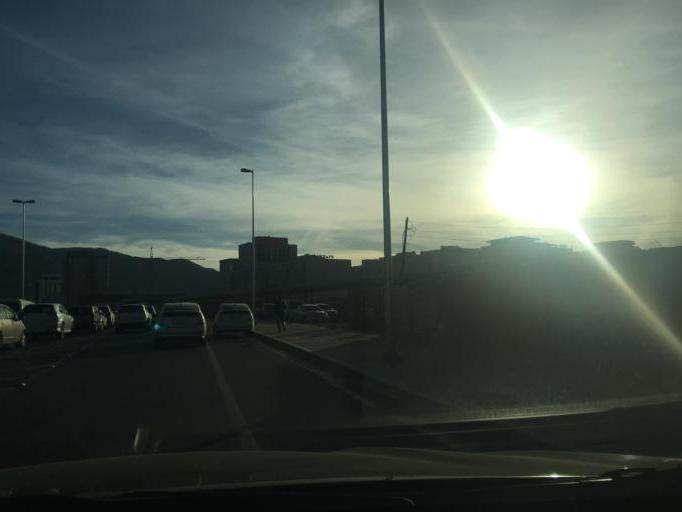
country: MN
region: Ulaanbaatar
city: Ulaanbaatar
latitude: 47.9050
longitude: 106.8935
